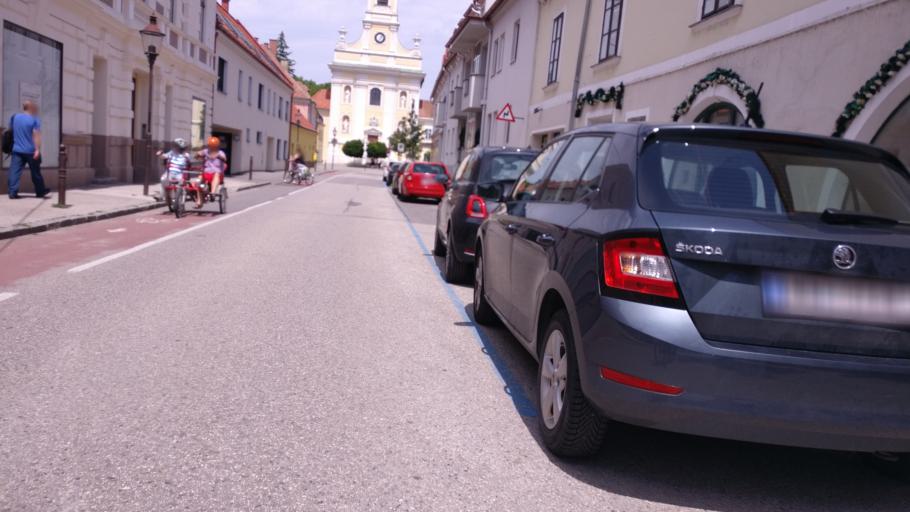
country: AT
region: Lower Austria
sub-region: Wiener Neustadt Stadt
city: Wiener Neustadt
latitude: 47.8177
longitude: 16.2453
